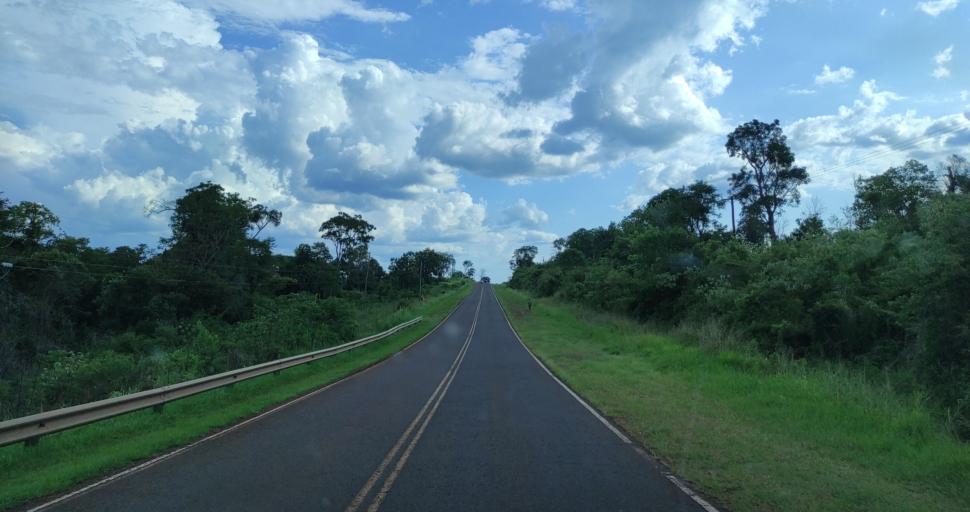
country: AR
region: Misiones
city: San Vicente
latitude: -26.3421
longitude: -54.1817
